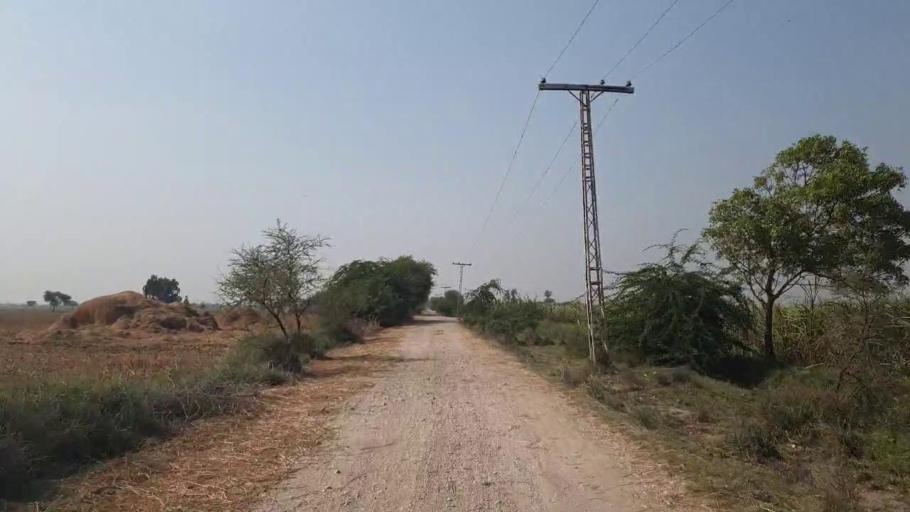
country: PK
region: Sindh
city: Matli
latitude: 24.9393
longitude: 68.5712
